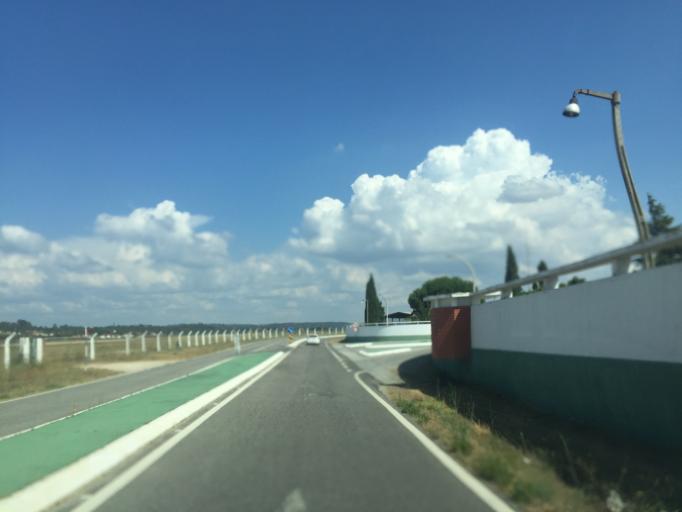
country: PT
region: Santarem
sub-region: Constancia
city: Constancia
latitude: 39.4727
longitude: -8.3717
